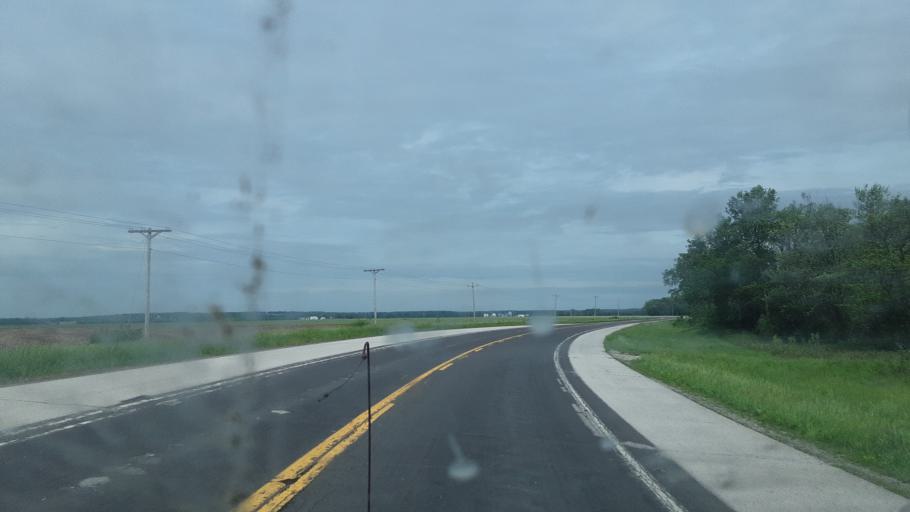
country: US
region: Illinois
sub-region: Hancock County
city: Warsaw
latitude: 40.3892
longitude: -91.5214
